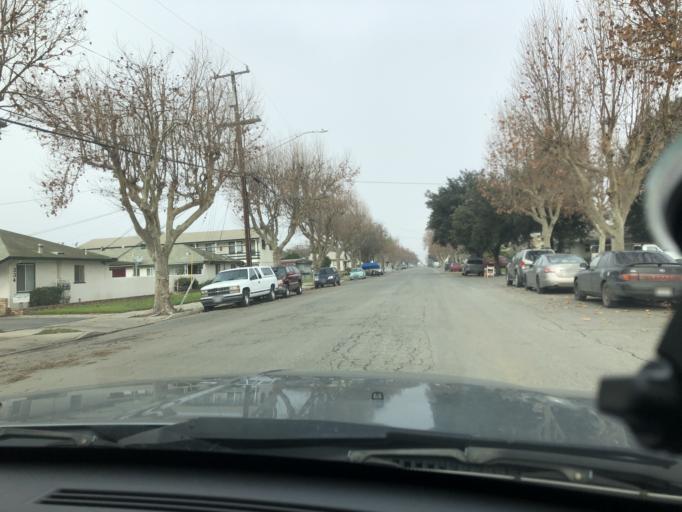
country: US
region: California
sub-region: Monterey County
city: King City
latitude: 36.2099
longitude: -121.1239
